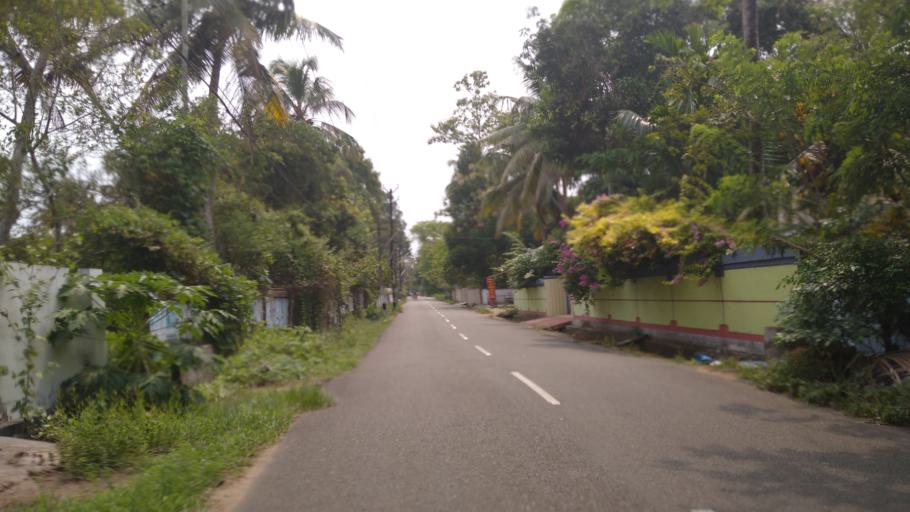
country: IN
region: Kerala
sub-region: Ernakulam
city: Elur
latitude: 10.1455
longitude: 76.2491
